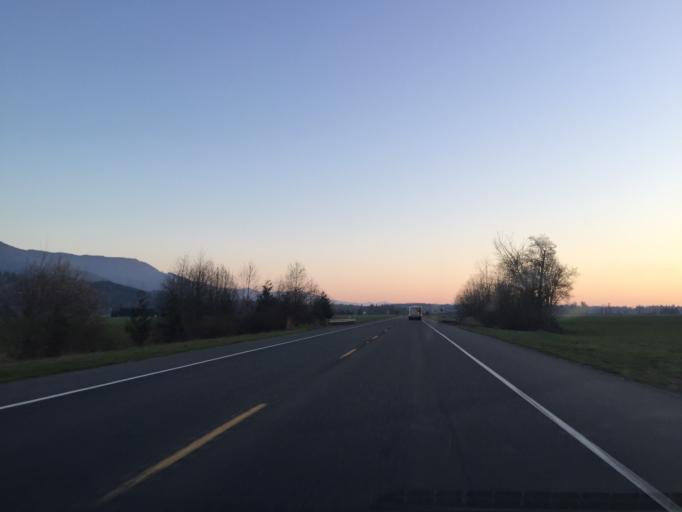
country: US
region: Washington
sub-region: Whatcom County
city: Sumas
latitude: 48.9725
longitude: -122.2725
